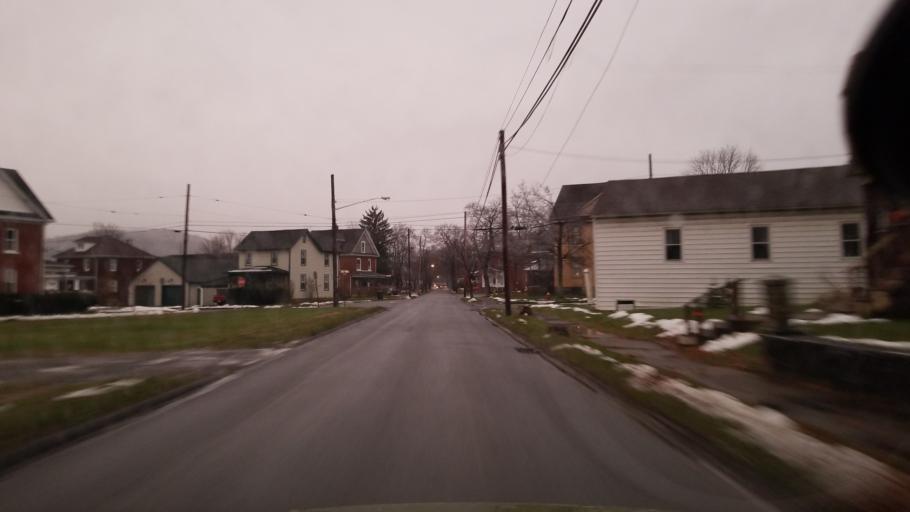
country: US
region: Pennsylvania
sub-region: Clearfield County
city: Clearfield
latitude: 41.0249
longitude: -78.4457
